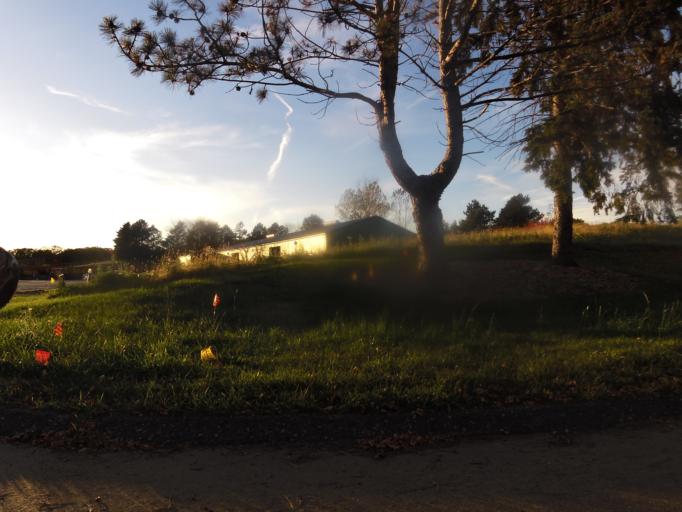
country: US
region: Minnesota
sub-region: Washington County
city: Lake Elmo
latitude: 44.9773
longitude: -92.8700
